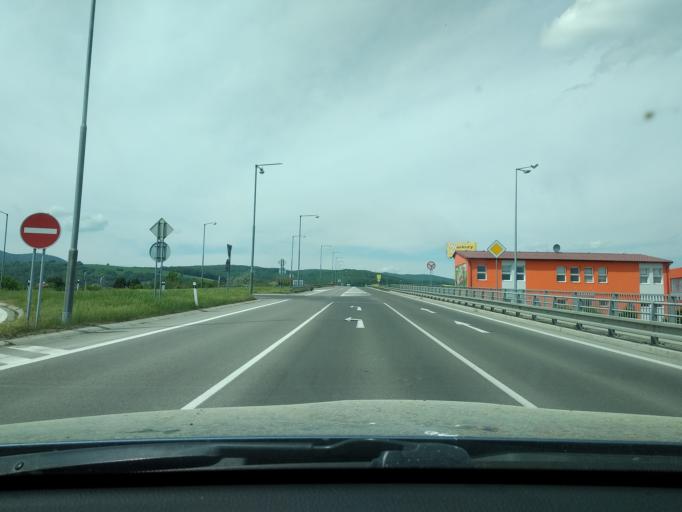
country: SK
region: Trenciansky
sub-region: Okres Trencin
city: Trencin
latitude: 48.8914
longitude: 18.0055
